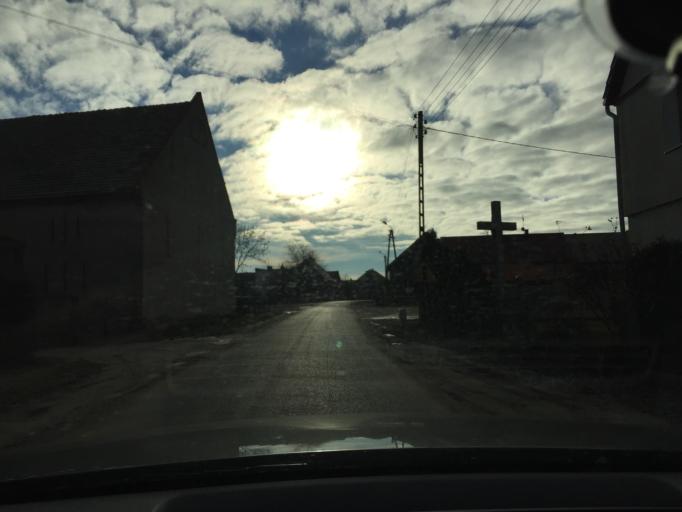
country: PL
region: Lower Silesian Voivodeship
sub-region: Powiat sredzki
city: Udanin
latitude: 51.0447
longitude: 16.5101
